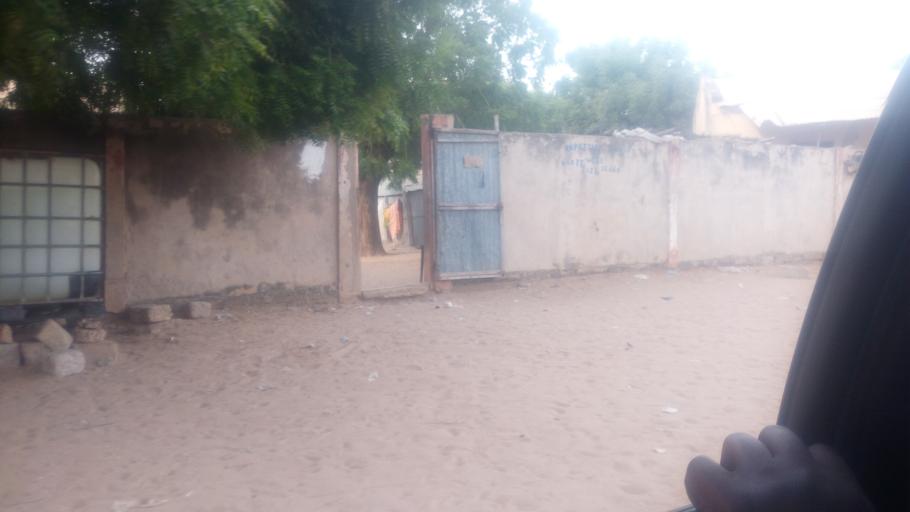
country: SN
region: Diourbel
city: Touba
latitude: 14.8660
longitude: -15.8828
